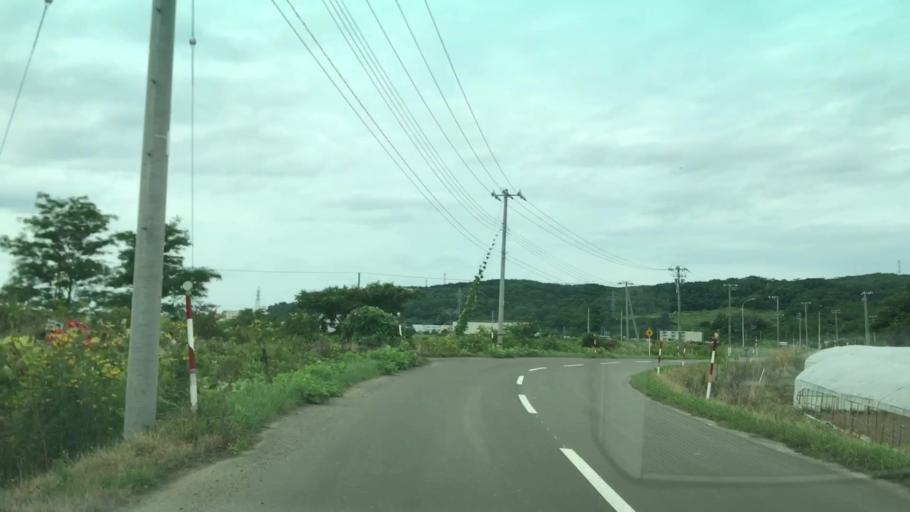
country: JP
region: Hokkaido
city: Iwanai
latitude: 43.0350
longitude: 140.5512
